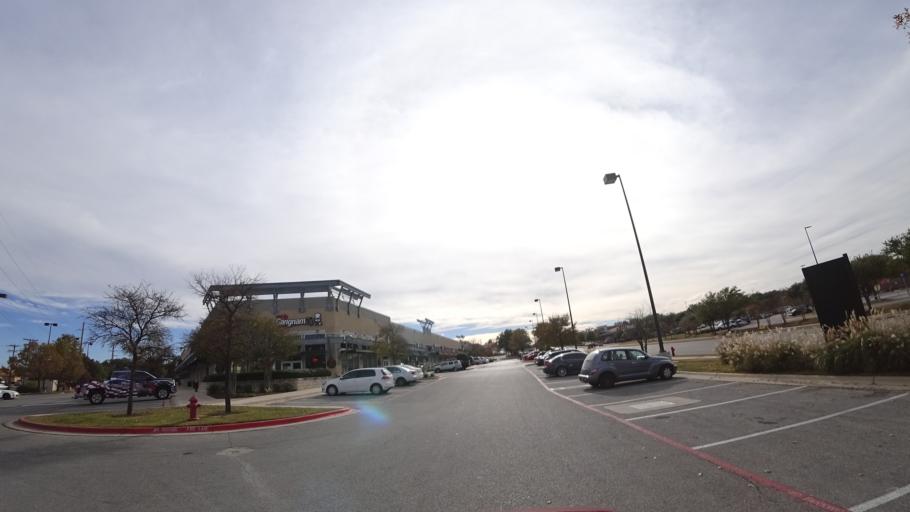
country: US
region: Texas
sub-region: Williamson County
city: Cedar Park
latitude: 30.5223
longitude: -97.8320
